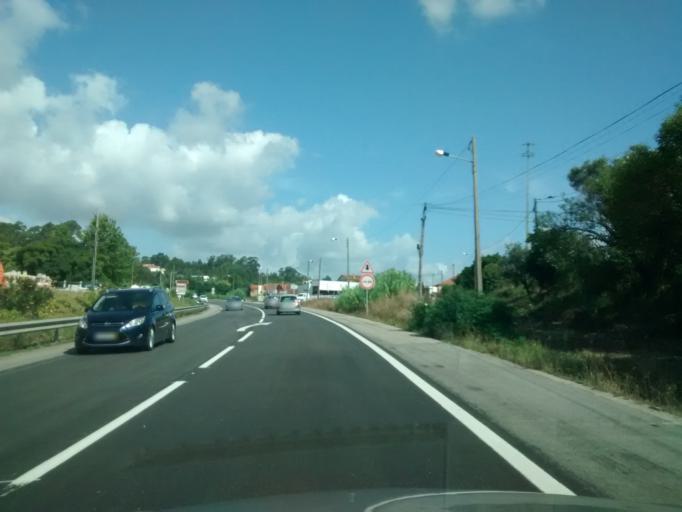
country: PT
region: Aveiro
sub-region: Oliveira do Bairro
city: Oliveira do Bairro
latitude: 40.5332
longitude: -8.5093
